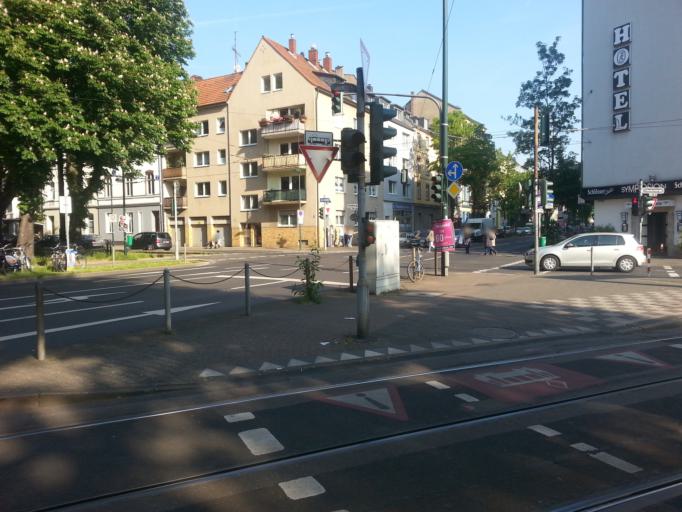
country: DE
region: North Rhine-Westphalia
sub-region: Regierungsbezirk Dusseldorf
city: Dusseldorf
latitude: 51.2474
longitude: 6.7835
